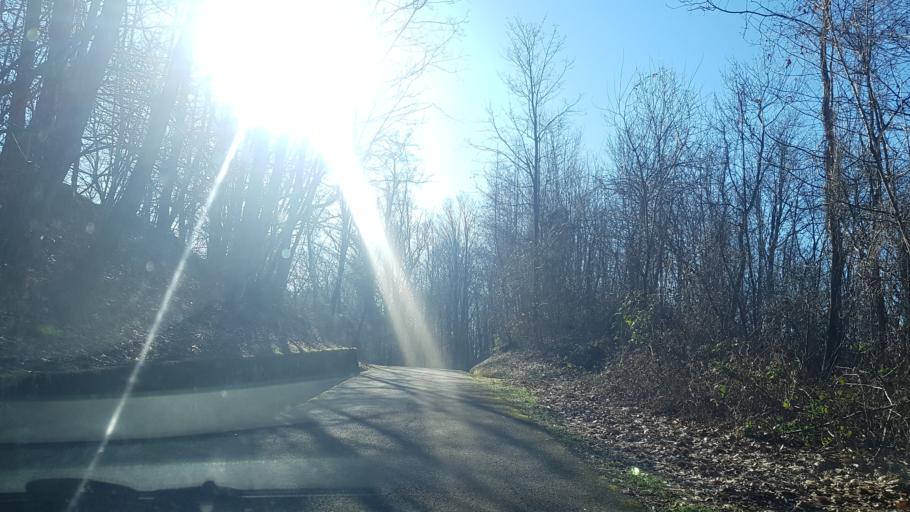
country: IT
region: Friuli Venezia Giulia
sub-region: Provincia di Udine
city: Isola
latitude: 46.2618
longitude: 13.2245
